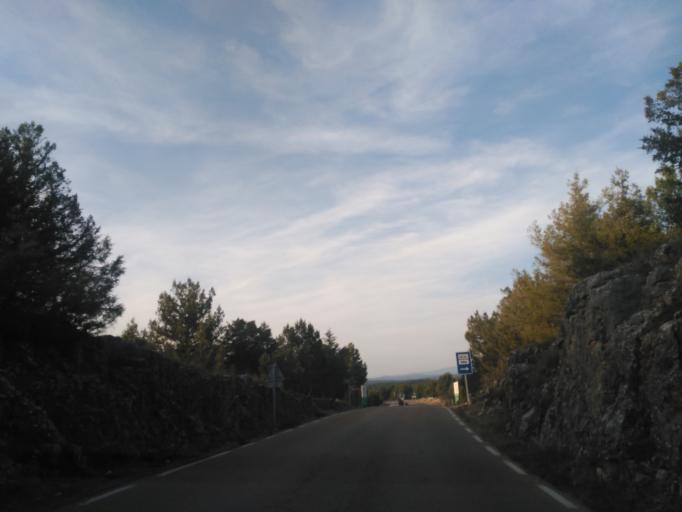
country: ES
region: Castille and Leon
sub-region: Provincia de Soria
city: Ucero
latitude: 41.7310
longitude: -3.0424
